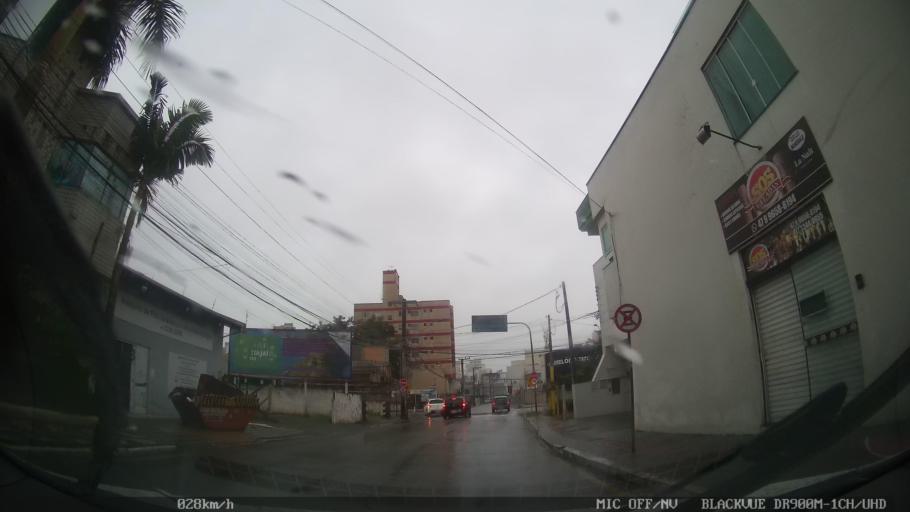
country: BR
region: Santa Catarina
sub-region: Itajai
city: Itajai
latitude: -26.9063
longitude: -48.6639
